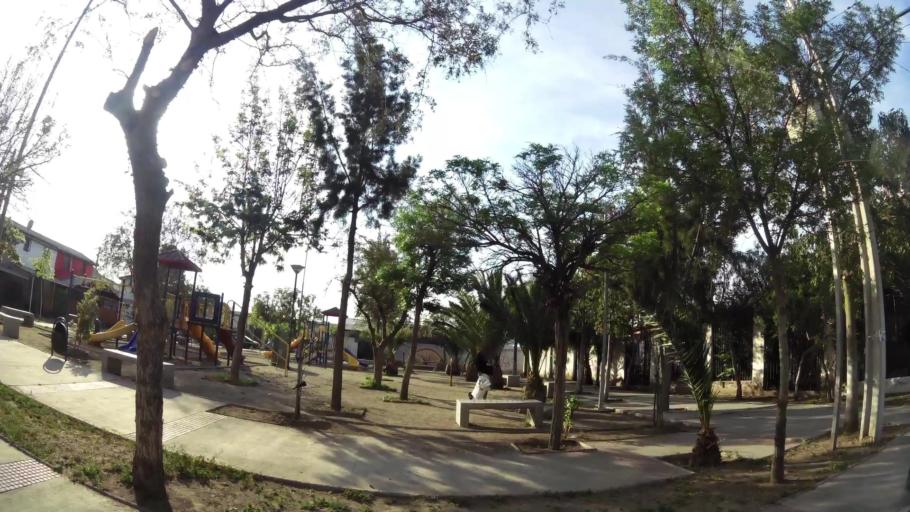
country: CL
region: Santiago Metropolitan
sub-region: Provincia de Santiago
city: Santiago
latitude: -33.5169
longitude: -70.6712
